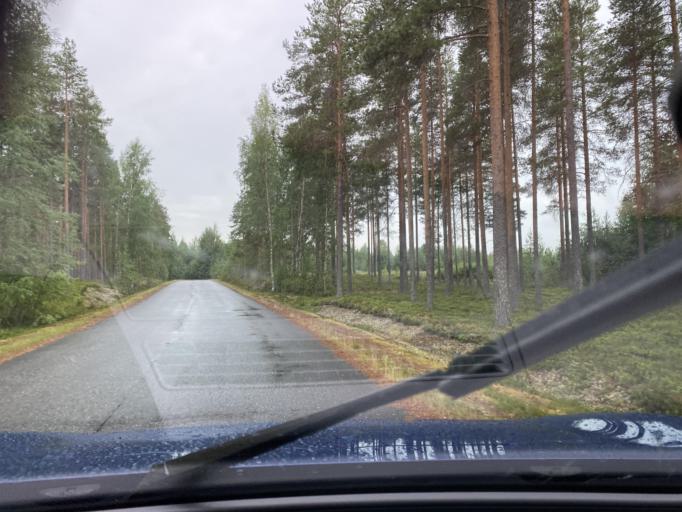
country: FI
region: Central Ostrobothnia
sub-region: Kaustinen
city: Halsua
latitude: 63.4137
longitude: 23.9749
